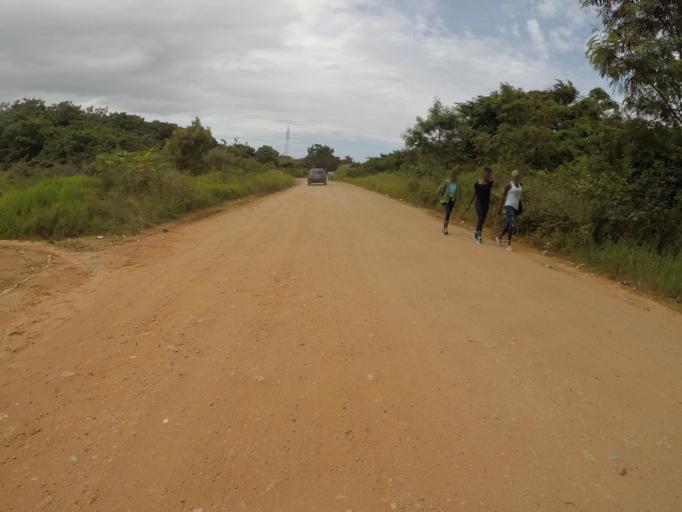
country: ZA
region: KwaZulu-Natal
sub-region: uThungulu District Municipality
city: eSikhawini
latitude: -28.8585
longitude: 31.9164
